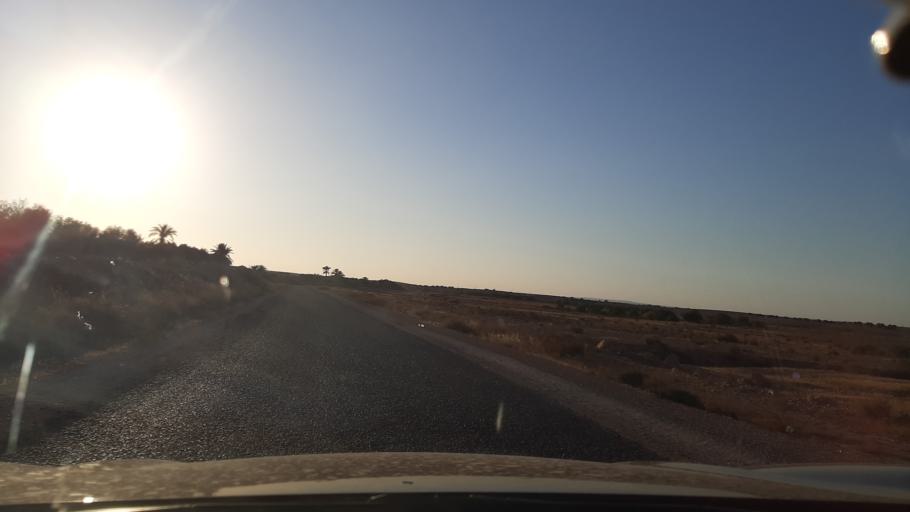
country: TN
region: Qabis
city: Matmata
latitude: 33.6233
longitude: 10.1383
